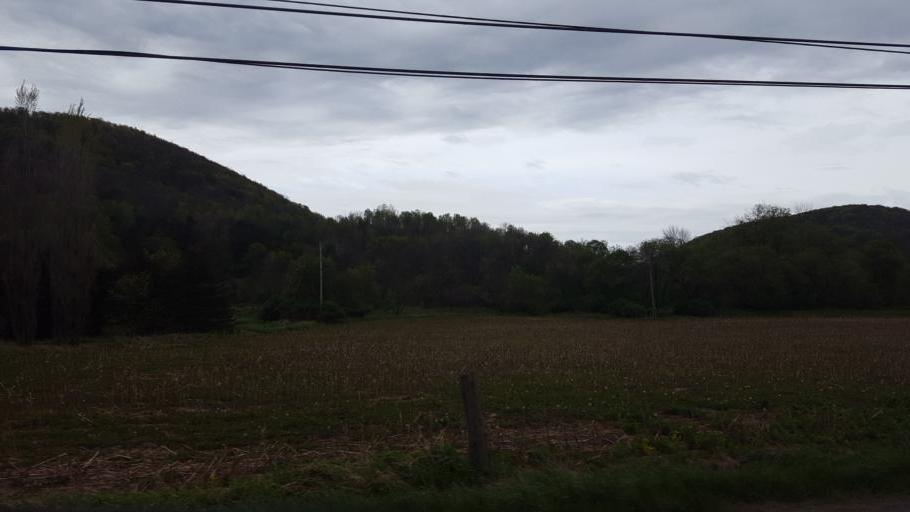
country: US
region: Pennsylvania
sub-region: Tioga County
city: Westfield
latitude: 41.9132
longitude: -77.5993
